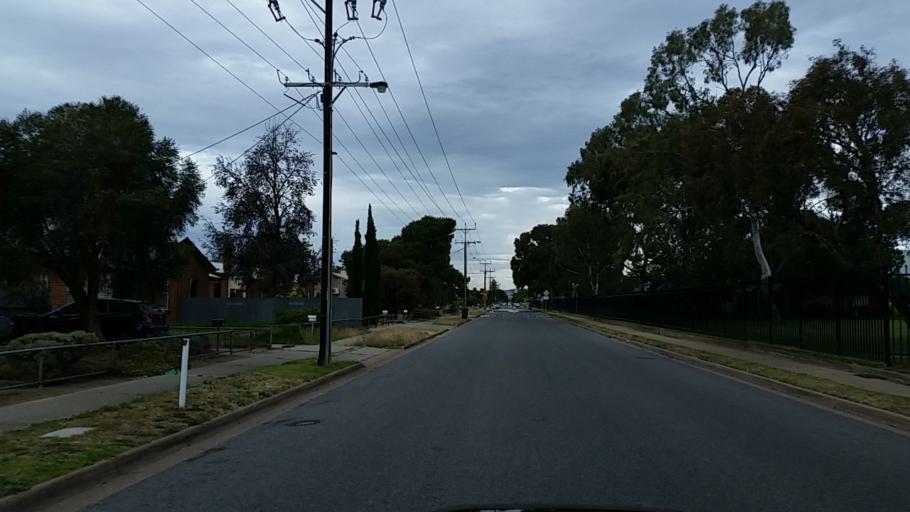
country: AU
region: South Australia
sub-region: Charles Sturt
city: Royal Park
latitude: -34.8850
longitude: 138.5056
